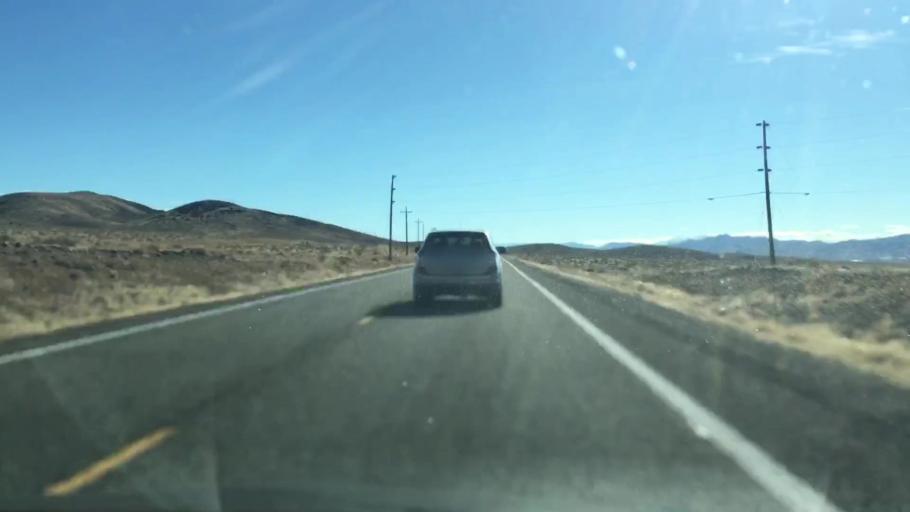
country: US
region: Nevada
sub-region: Lyon County
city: Yerington
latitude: 39.1977
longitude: -119.2130
